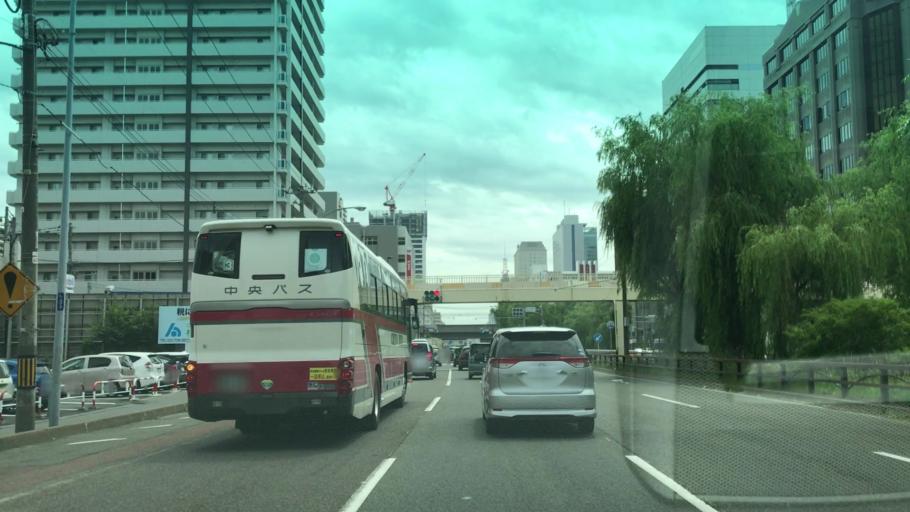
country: JP
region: Hokkaido
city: Sapporo
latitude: 43.0716
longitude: 141.3546
